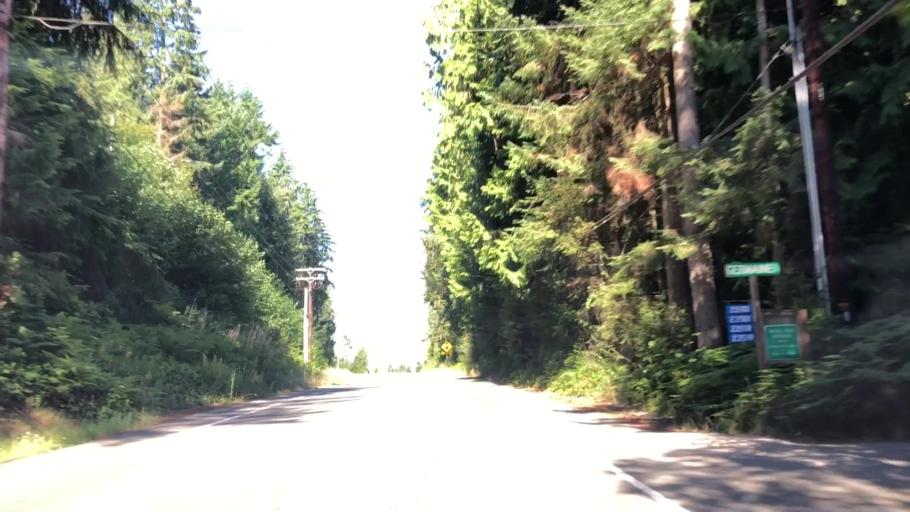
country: US
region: Washington
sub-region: Kitsap County
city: Kingston
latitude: 47.7730
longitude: -122.5122
